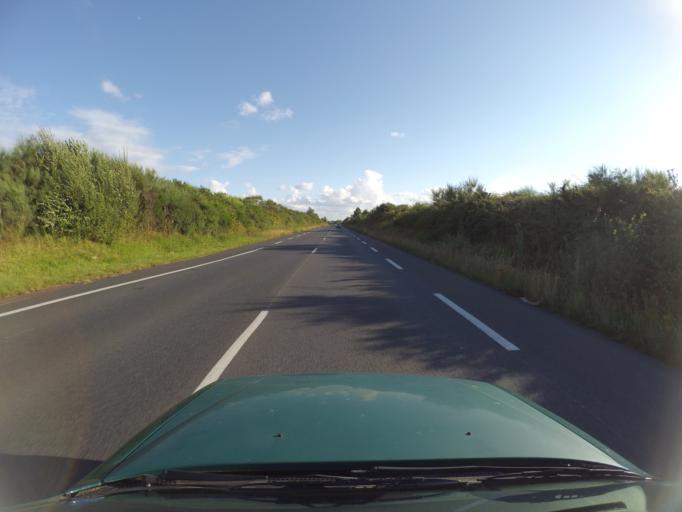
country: FR
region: Pays de la Loire
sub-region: Departement de la Vendee
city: Saint-Hilaire-de-Loulay
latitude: 47.0034
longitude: -1.3437
